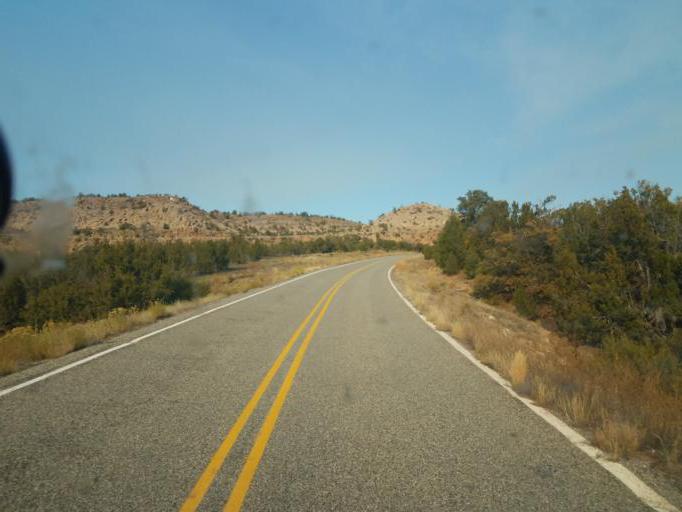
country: US
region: New Mexico
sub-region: Los Alamos County
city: White Rock
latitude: 35.8091
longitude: -106.2484
